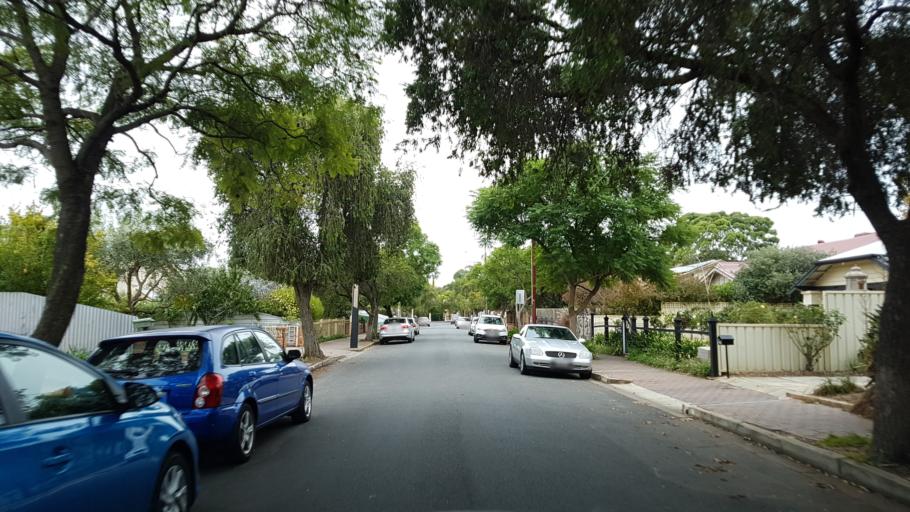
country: AU
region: South Australia
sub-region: Unley
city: Forestville
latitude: -34.9606
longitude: 138.5788
